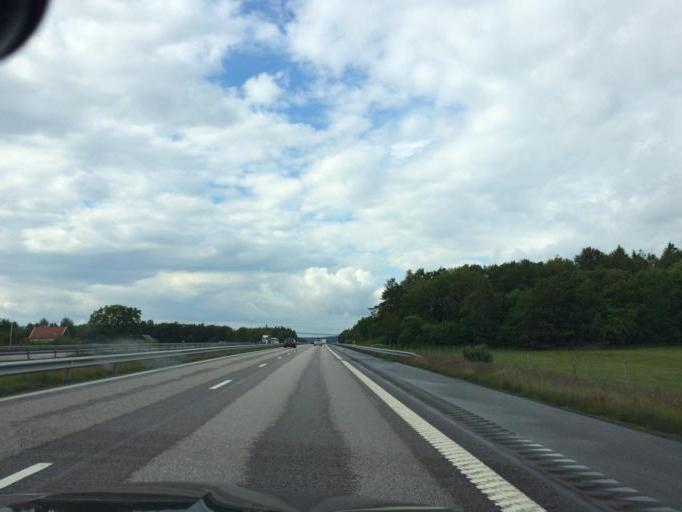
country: SE
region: Halland
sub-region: Kungsbacka Kommun
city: Frillesas
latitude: 57.2755
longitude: 12.2156
